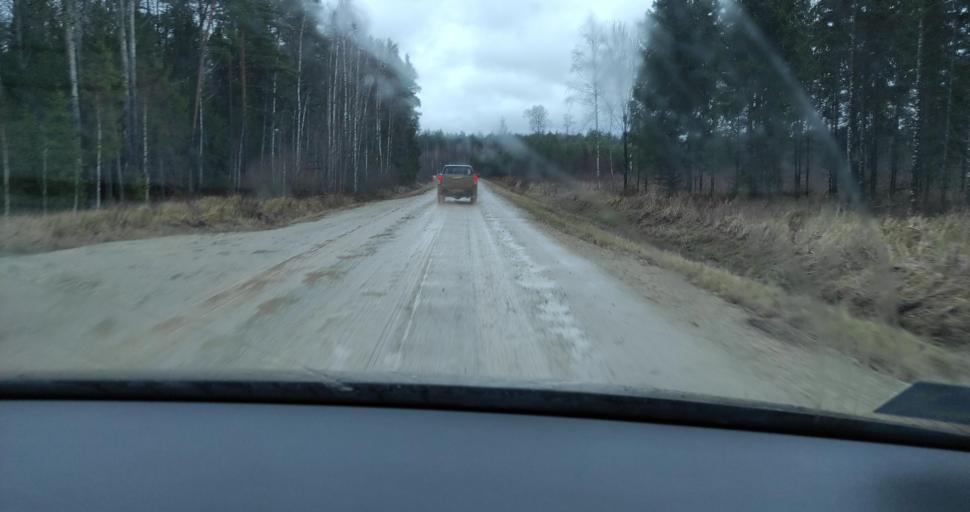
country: LV
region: Skrunda
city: Skrunda
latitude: 56.5596
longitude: 22.1235
